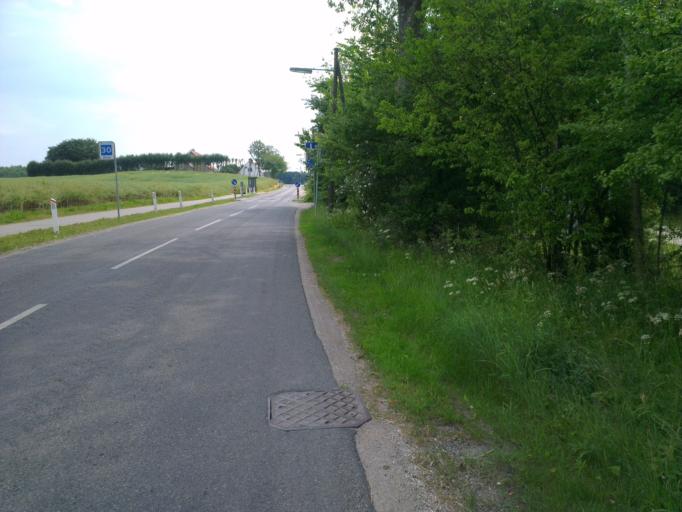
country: DK
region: Capital Region
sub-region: Allerod Kommune
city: Lillerod
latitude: 55.8999
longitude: 12.3363
